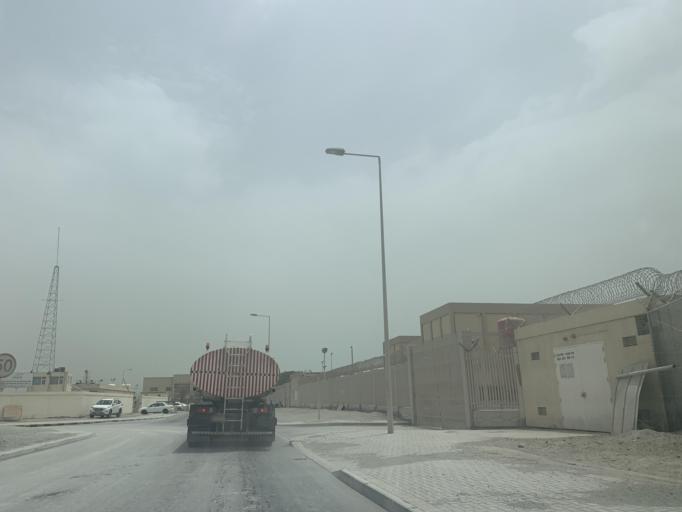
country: BH
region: Northern
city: Sitrah
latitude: 26.1852
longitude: 50.6210
